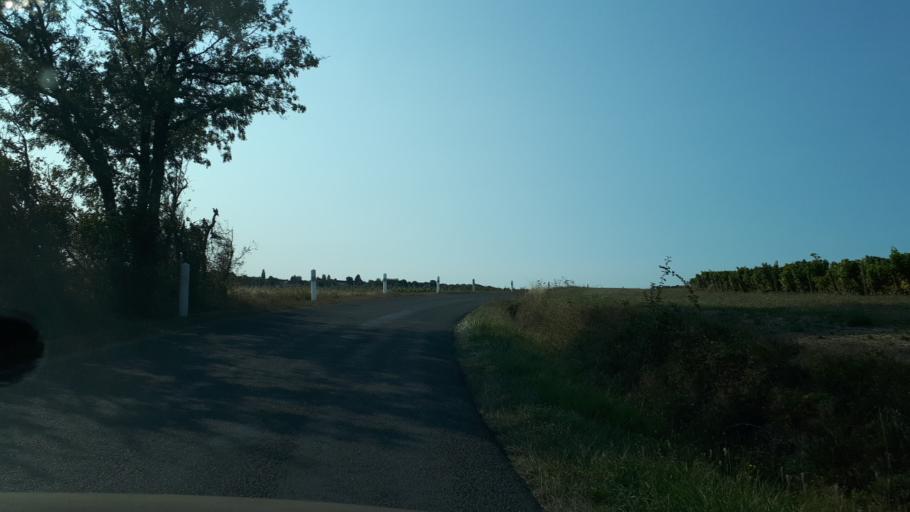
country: FR
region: Centre
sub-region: Departement du Cher
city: Menetou-Salon
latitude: 47.2271
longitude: 2.5206
